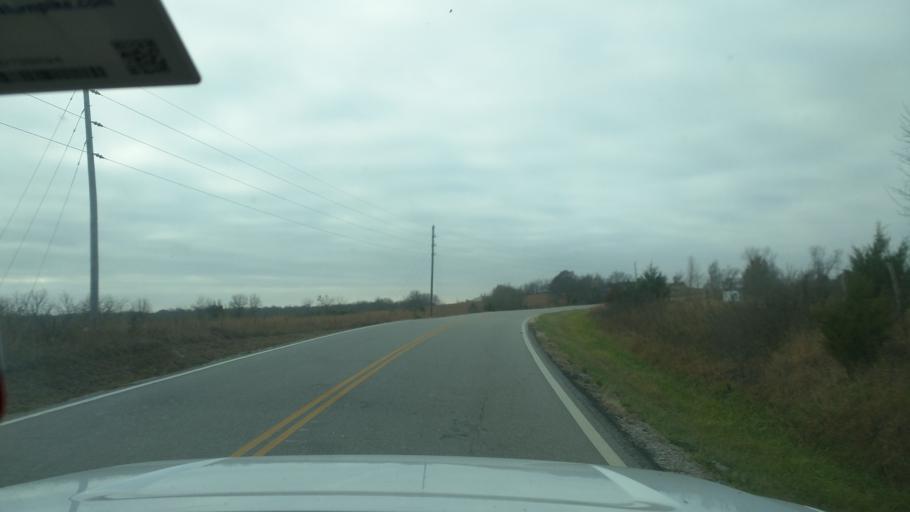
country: US
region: Kansas
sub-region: Greenwood County
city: Eureka
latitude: 37.6982
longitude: -96.2232
